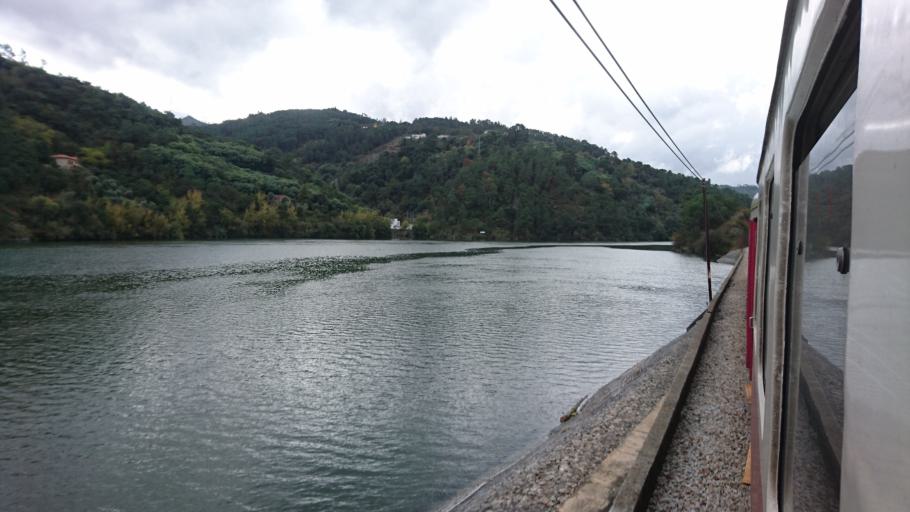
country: PT
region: Viseu
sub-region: Resende
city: Resende
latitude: 41.0989
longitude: -8.0237
